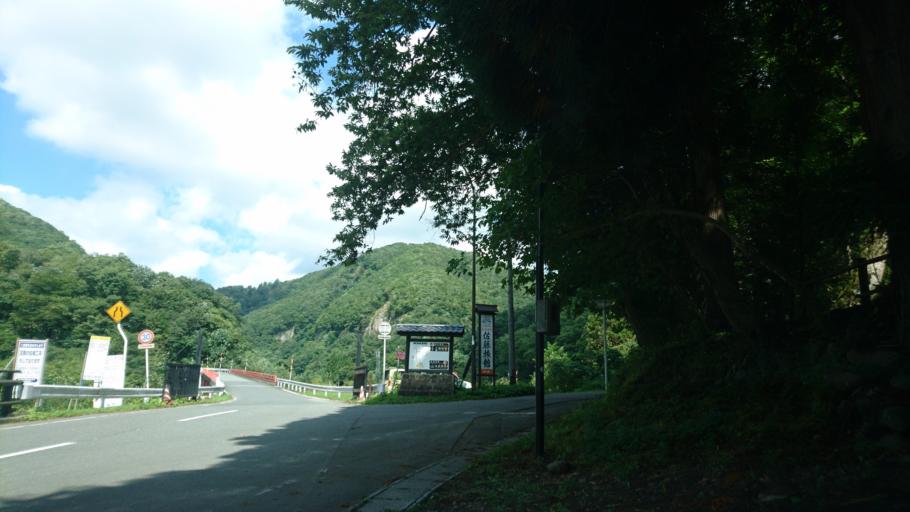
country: JP
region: Miyagi
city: Furukawa
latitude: 38.8617
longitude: 140.7776
